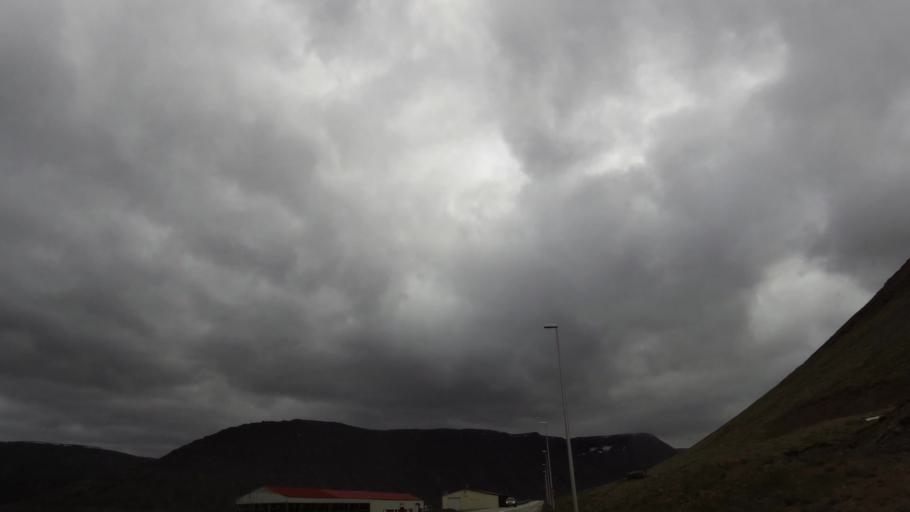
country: IS
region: Westfjords
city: Isafjoerdur
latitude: 66.1060
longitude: -23.1102
